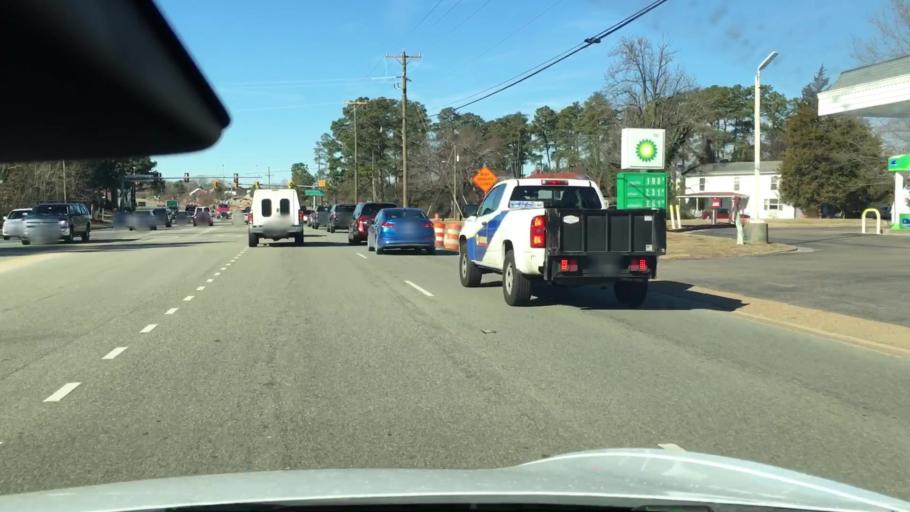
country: US
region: Virginia
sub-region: Chesterfield County
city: Brandermill
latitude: 37.5058
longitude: -77.6607
